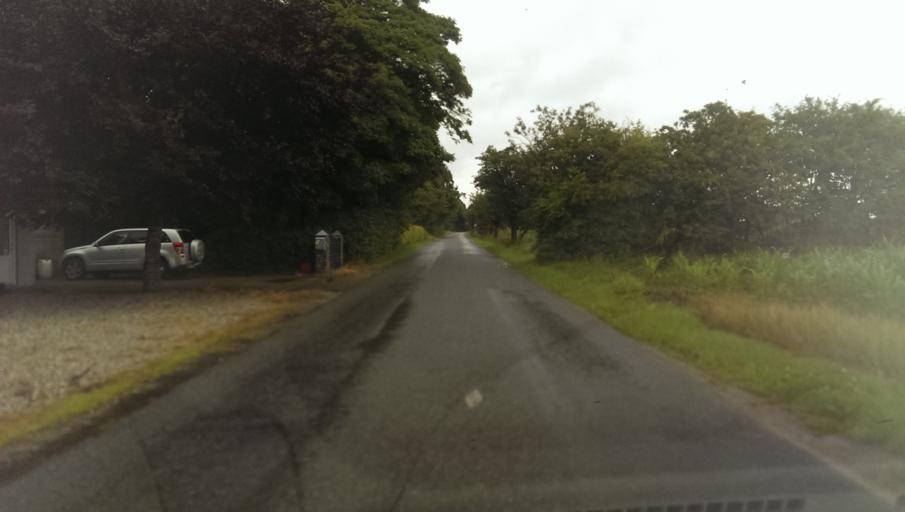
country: DK
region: South Denmark
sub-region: Esbjerg Kommune
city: Bramming
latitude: 55.4907
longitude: 8.6575
